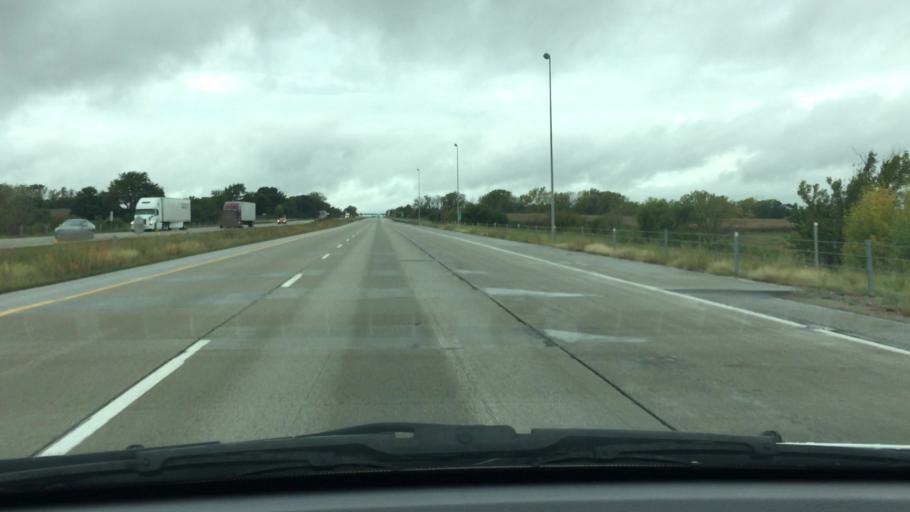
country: US
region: Iowa
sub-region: Polk County
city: Mitchellville
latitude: 41.6810
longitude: -93.3449
